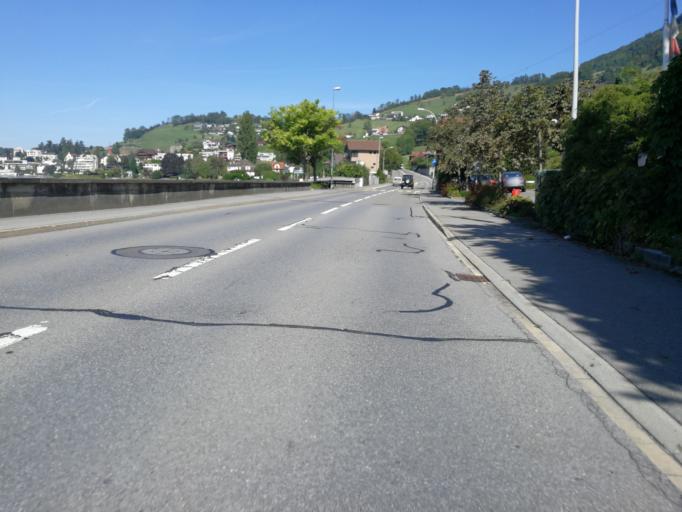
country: CH
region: Lucerne
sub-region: Lucerne-Land District
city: Weggis
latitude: 47.0285
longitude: 8.4476
